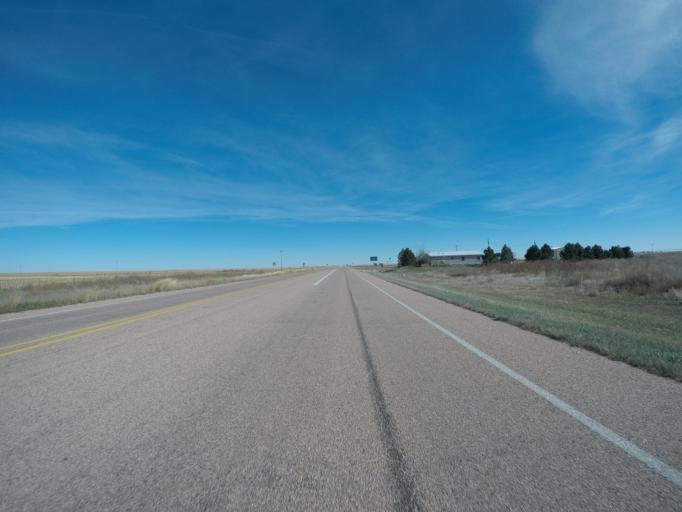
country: US
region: Colorado
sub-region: Kit Carson County
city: Burlington
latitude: 39.6563
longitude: -102.5946
